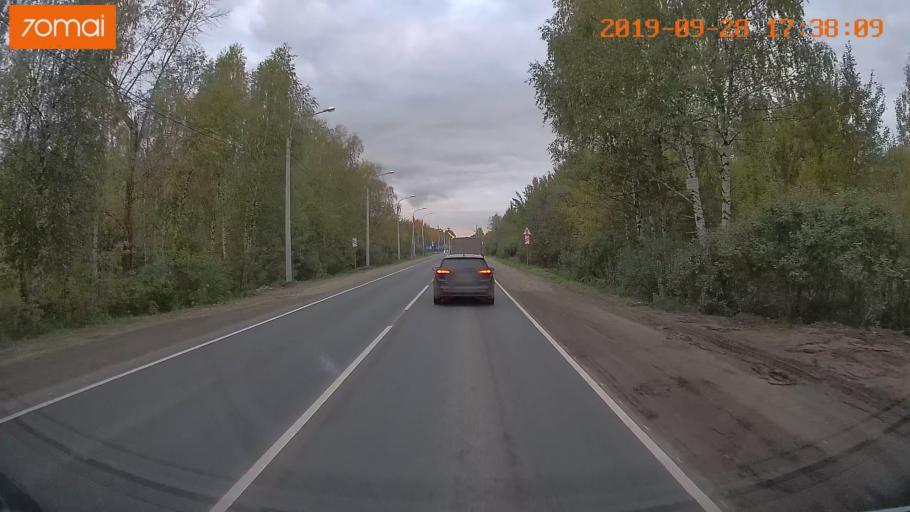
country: RU
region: Jaroslavl
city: Yaroslavl
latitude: 57.5433
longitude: 39.9400
